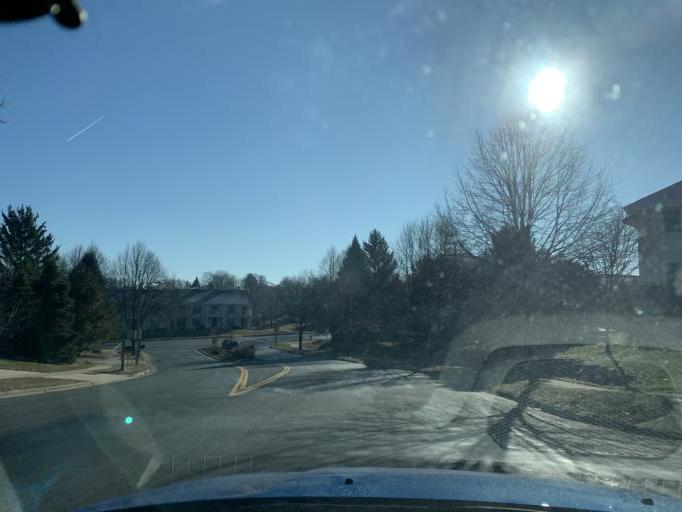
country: US
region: Wisconsin
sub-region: Dane County
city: Middleton
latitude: 43.0439
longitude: -89.5051
